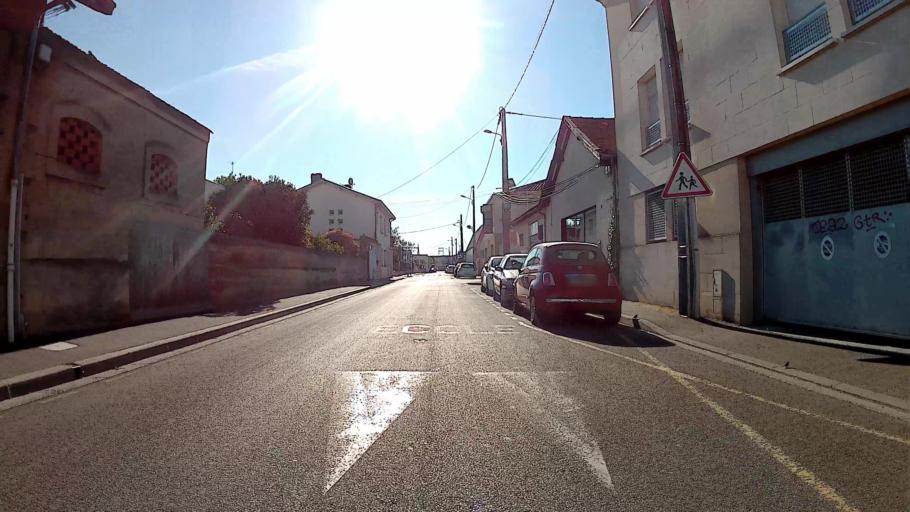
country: FR
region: Aquitaine
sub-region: Departement de la Gironde
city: Begles
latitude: 44.8165
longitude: -0.5454
